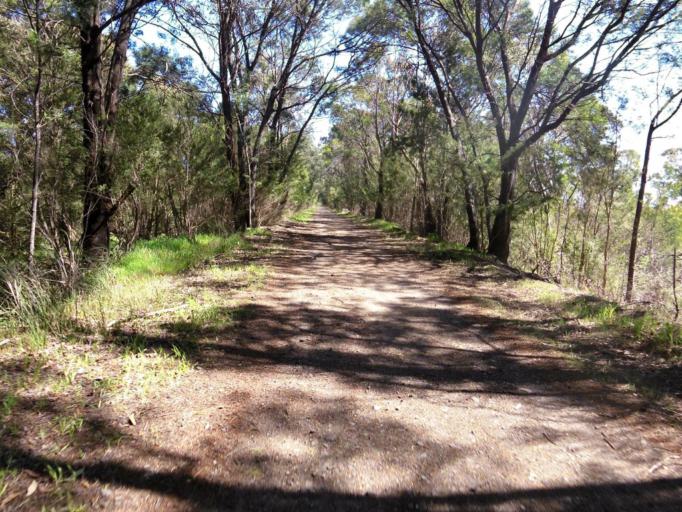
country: AU
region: Victoria
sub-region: Latrobe
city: Moe
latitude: -38.1684
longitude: 146.3240
